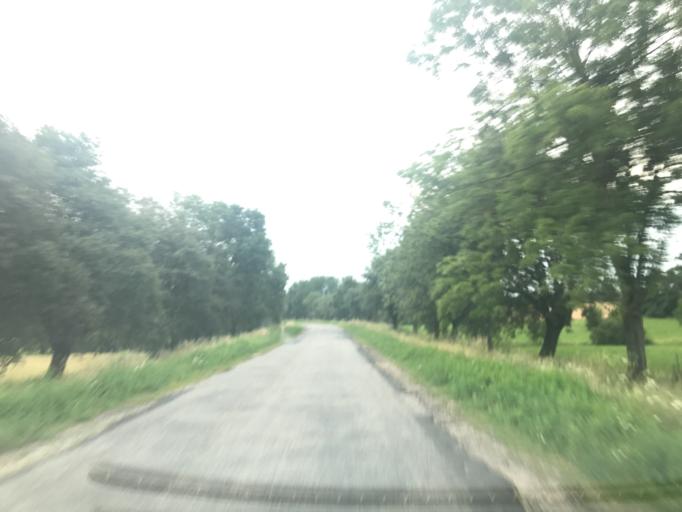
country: PL
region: Kujawsko-Pomorskie
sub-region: Powiat lipnowski
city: Lipno
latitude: 52.7923
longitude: 19.2084
